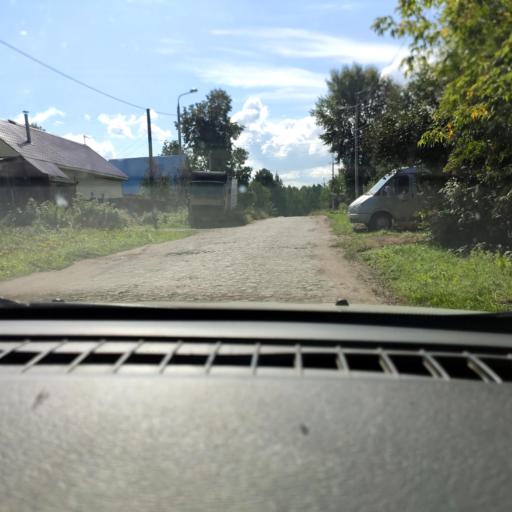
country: RU
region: Perm
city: Polazna
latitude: 58.1172
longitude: 56.3937
